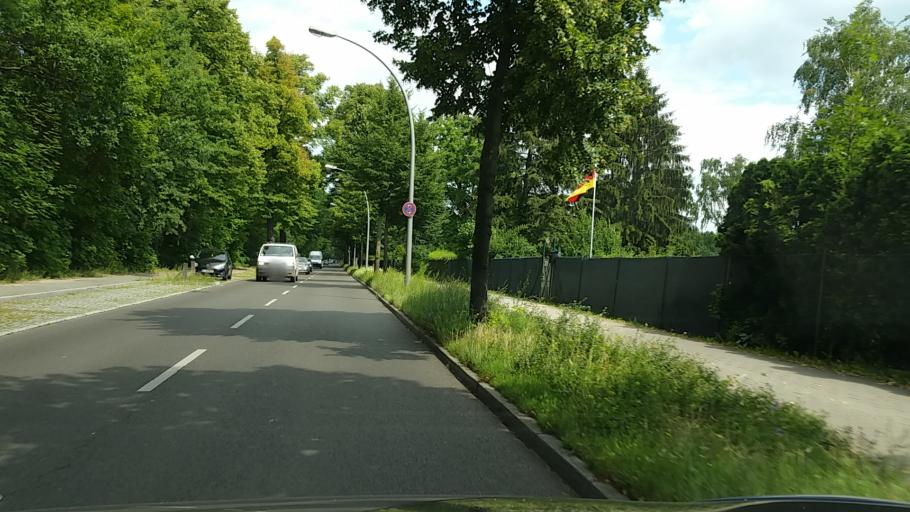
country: DE
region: Berlin
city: Siemensstadt
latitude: 52.5479
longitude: 13.2543
